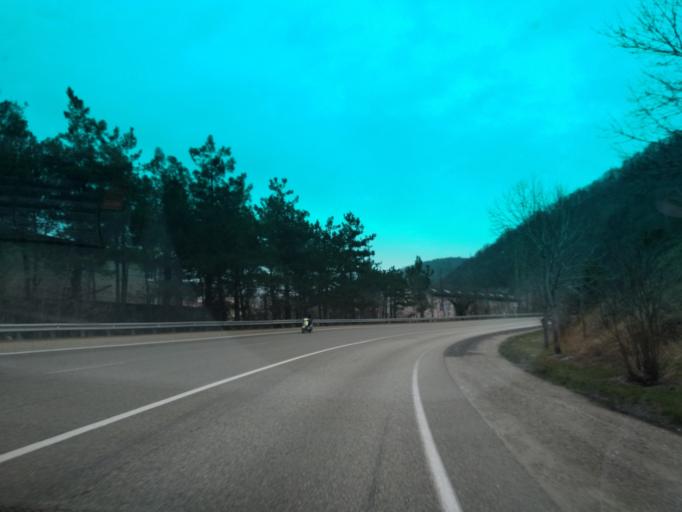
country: RU
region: Krasnodarskiy
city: Ol'ginka
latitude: 44.1932
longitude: 38.8895
